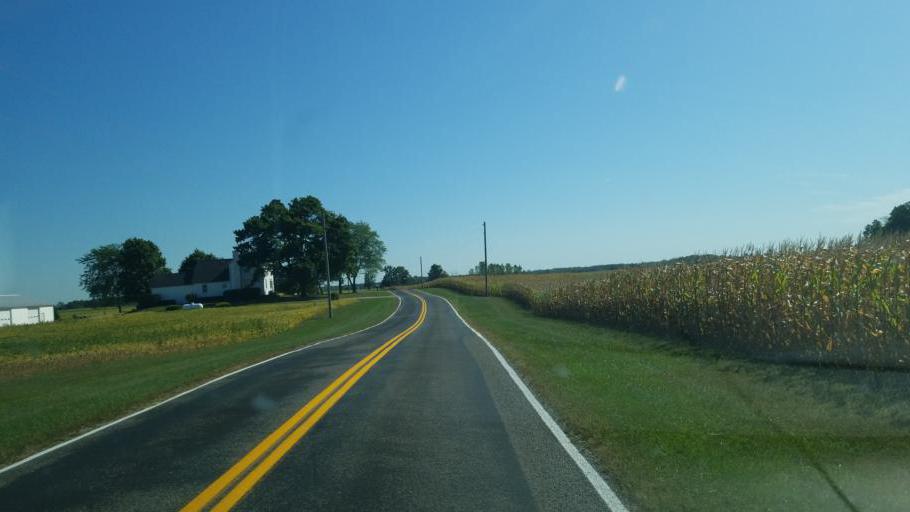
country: US
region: Ohio
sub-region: Champaign County
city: Mechanicsburg
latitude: 40.1417
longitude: -83.6013
